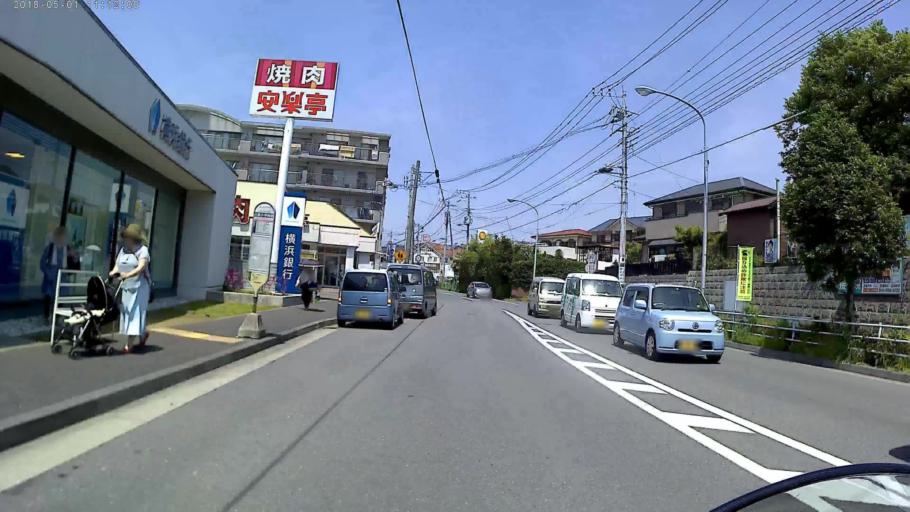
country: JP
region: Kanagawa
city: Minami-rinkan
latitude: 35.4880
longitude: 139.5426
